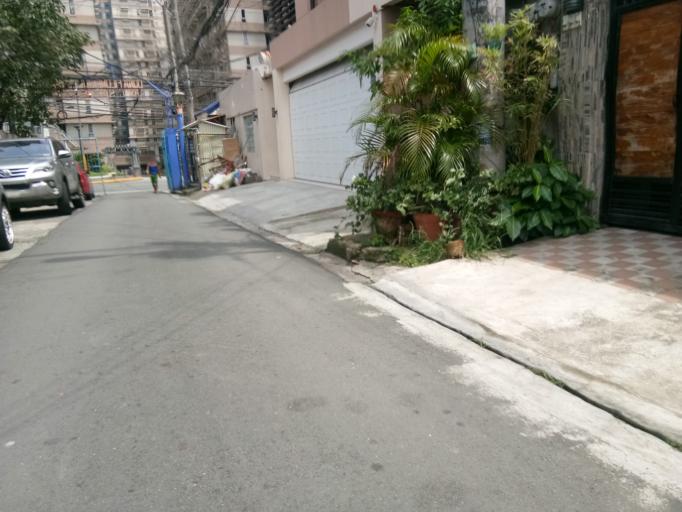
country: PH
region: Metro Manila
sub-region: San Juan
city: San Juan
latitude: 14.6085
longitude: 121.0470
